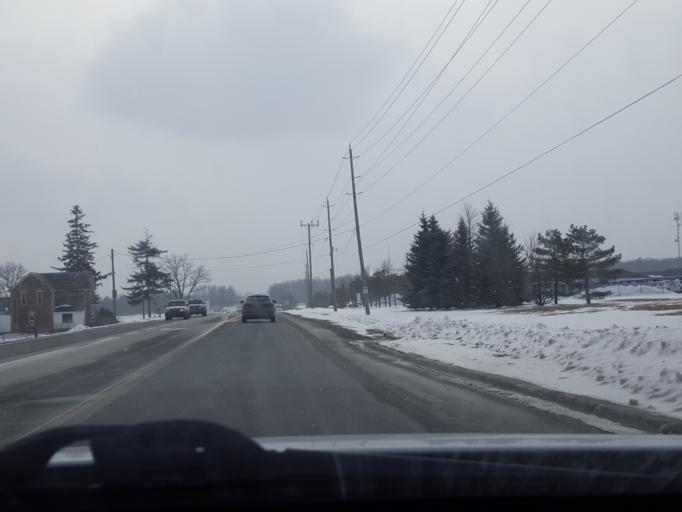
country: CA
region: Ontario
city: Uxbridge
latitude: 44.0175
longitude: -79.2320
